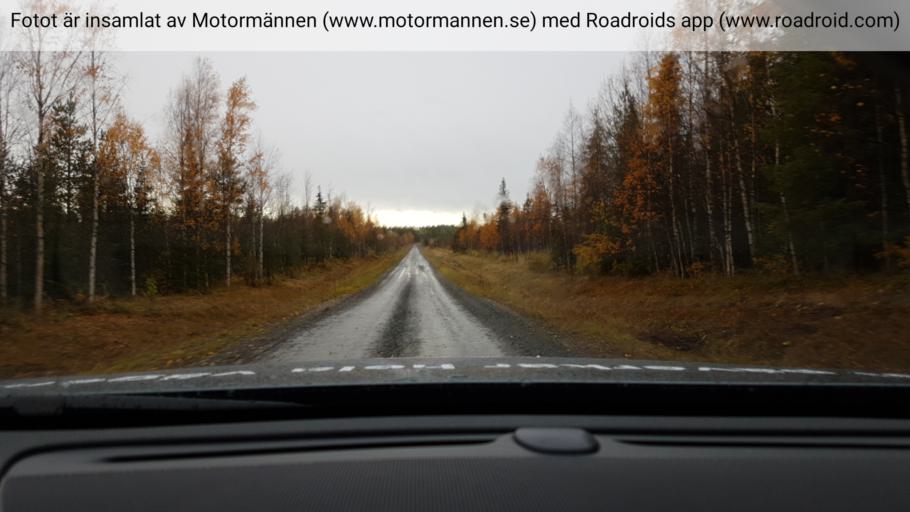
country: SE
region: Norrbotten
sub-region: Pajala Kommun
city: Pajala
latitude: 66.9797
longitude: 22.8868
